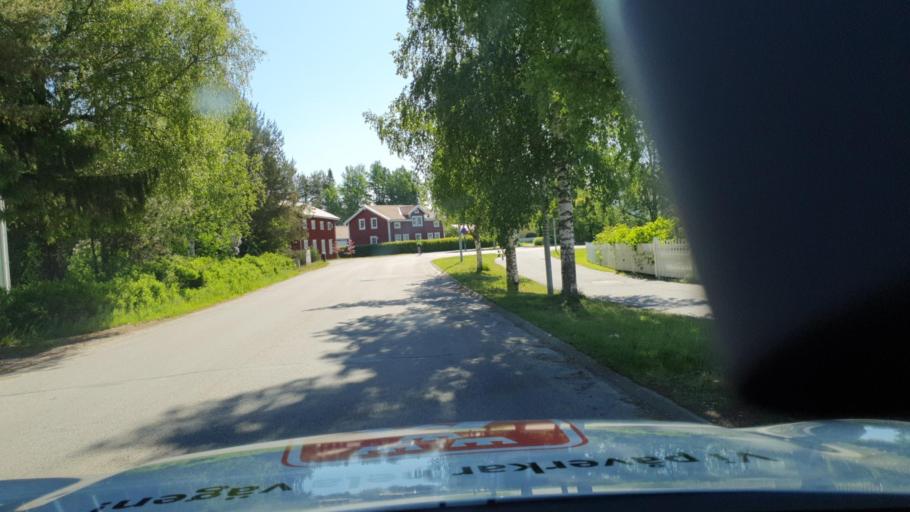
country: SE
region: Vaesterbotten
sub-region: Umea Kommun
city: Roback
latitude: 63.8388
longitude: 20.2051
